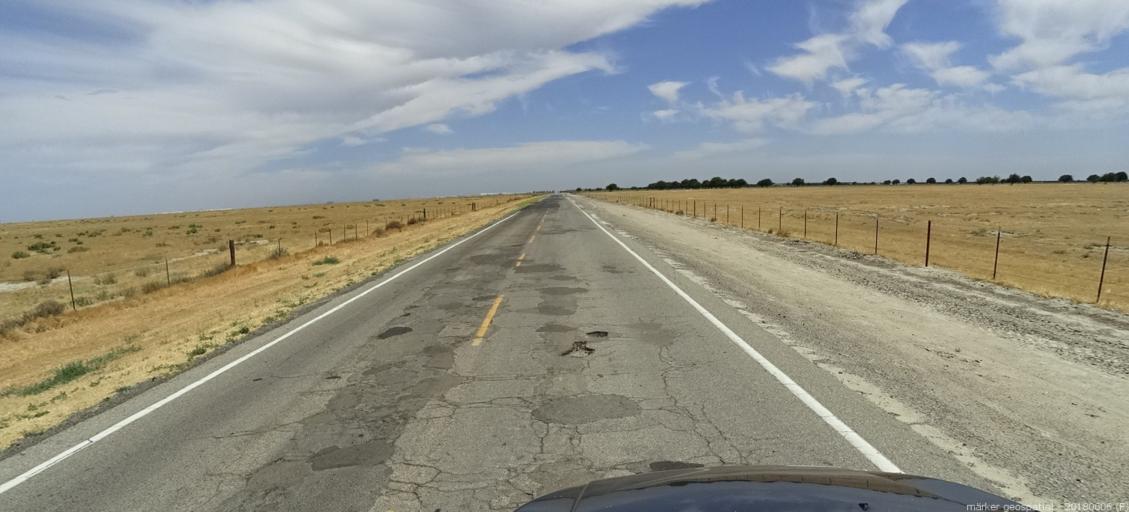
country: US
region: California
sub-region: Fresno County
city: Firebaugh
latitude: 36.8973
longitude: -120.3819
